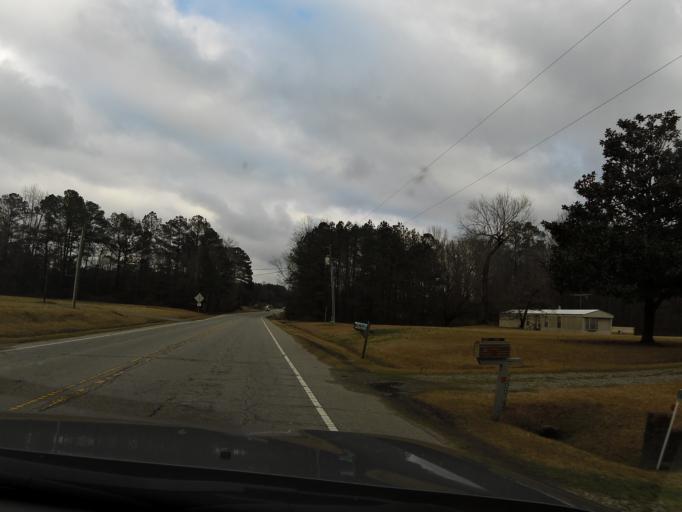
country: US
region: North Carolina
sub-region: Nash County
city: Rocky Mount
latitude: 35.8644
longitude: -77.7180
